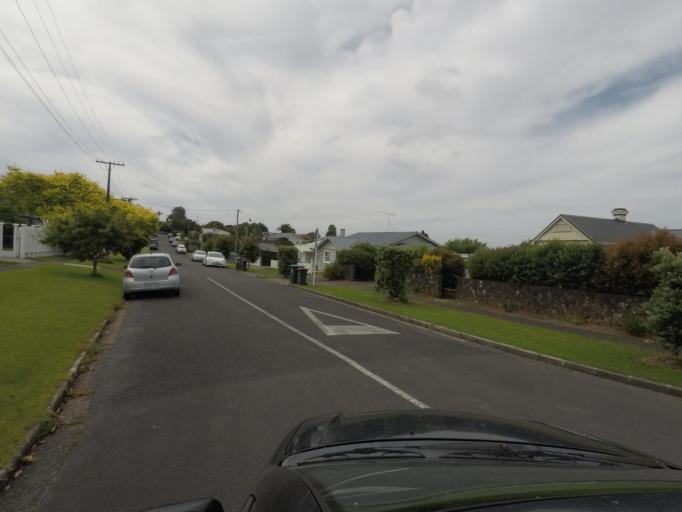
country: NZ
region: Auckland
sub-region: Auckland
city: Auckland
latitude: -36.8856
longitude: 174.7232
